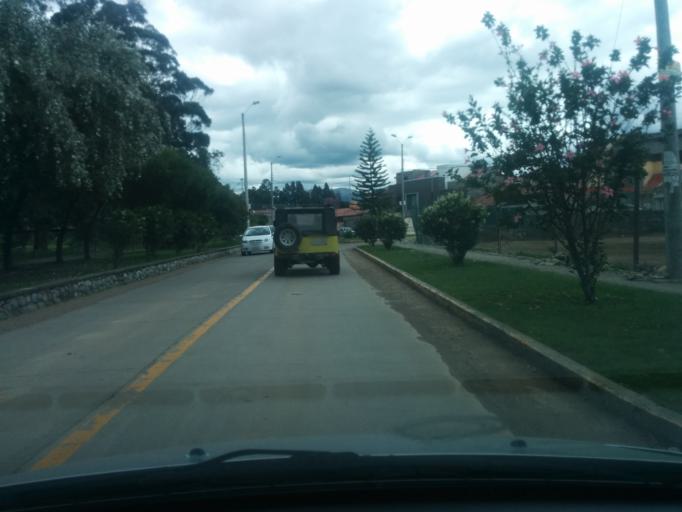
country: EC
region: Azuay
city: Cuenca
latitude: -2.8915
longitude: -78.9612
